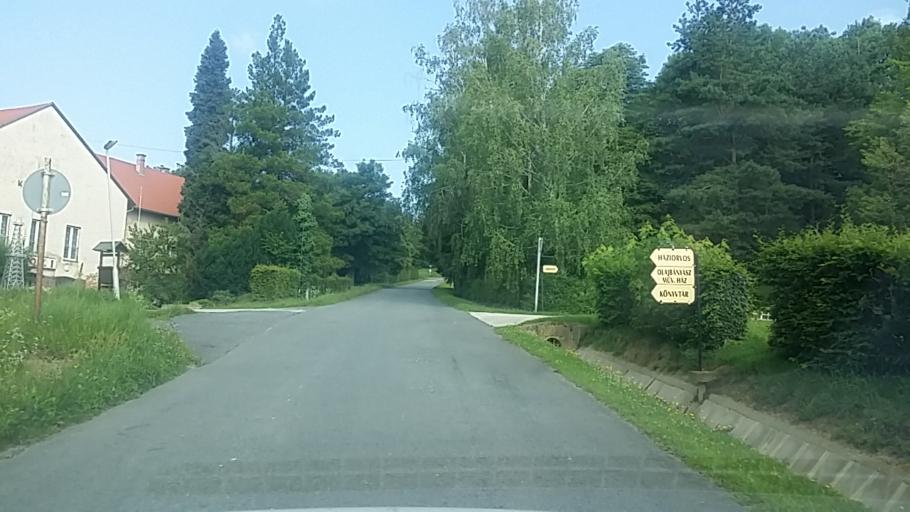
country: HU
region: Zala
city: Lenti
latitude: 46.5549
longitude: 16.5510
